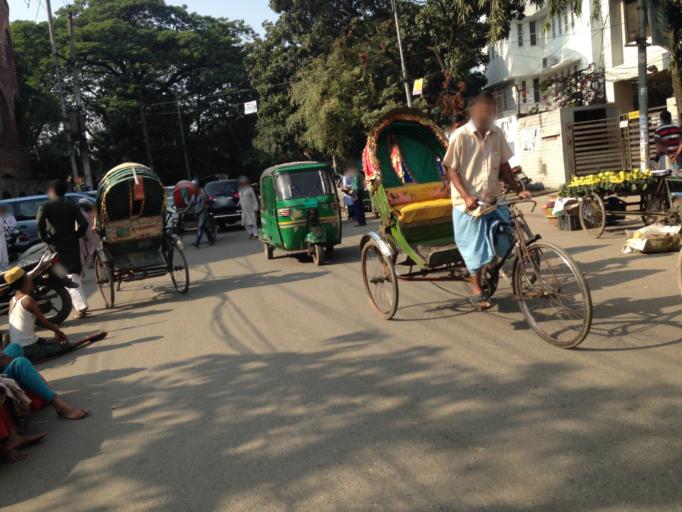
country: BD
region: Dhaka
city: Azimpur
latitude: 23.7444
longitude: 90.3792
